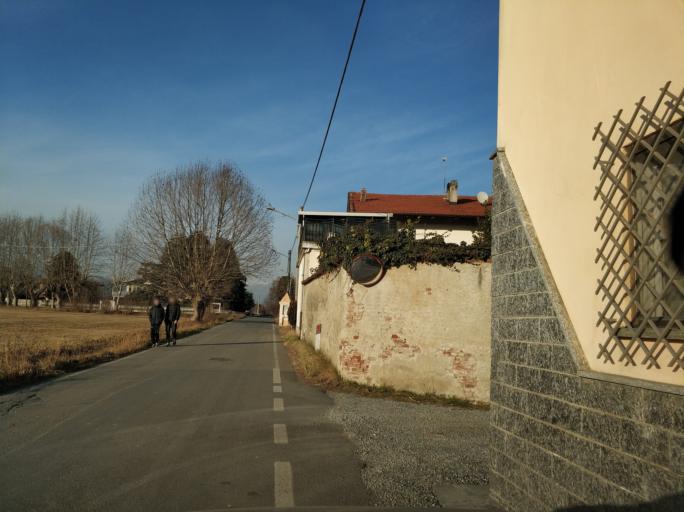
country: IT
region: Piedmont
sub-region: Provincia di Torino
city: San Francesco al Campo
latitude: 45.2066
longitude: 7.6550
